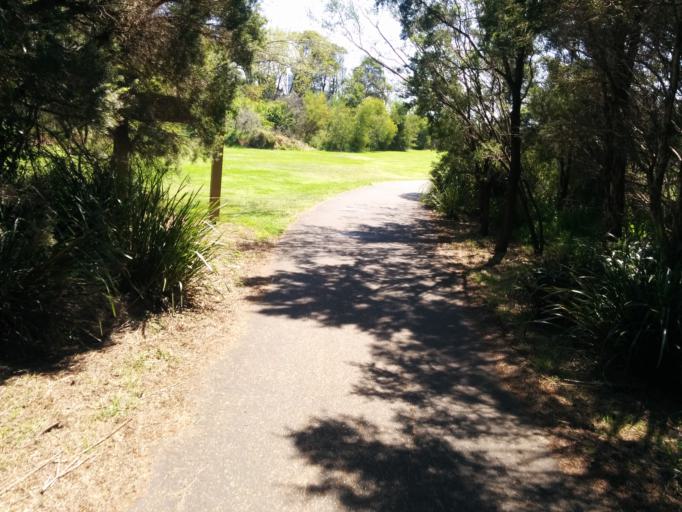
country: AU
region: New South Wales
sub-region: Canada Bay
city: Concord West
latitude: -33.8565
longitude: 151.0834
